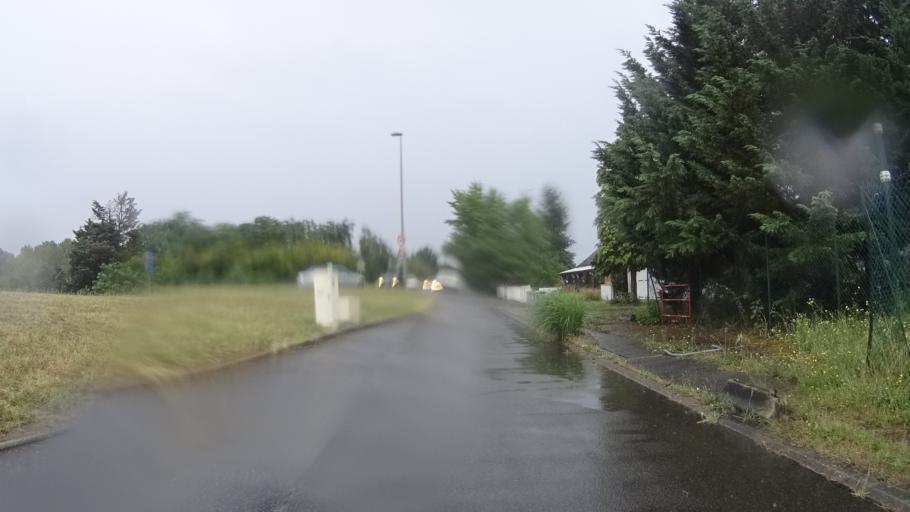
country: FR
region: Centre
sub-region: Departement du Loiret
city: Saint-Pryve-Saint-Mesmin
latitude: 47.8927
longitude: 1.8761
